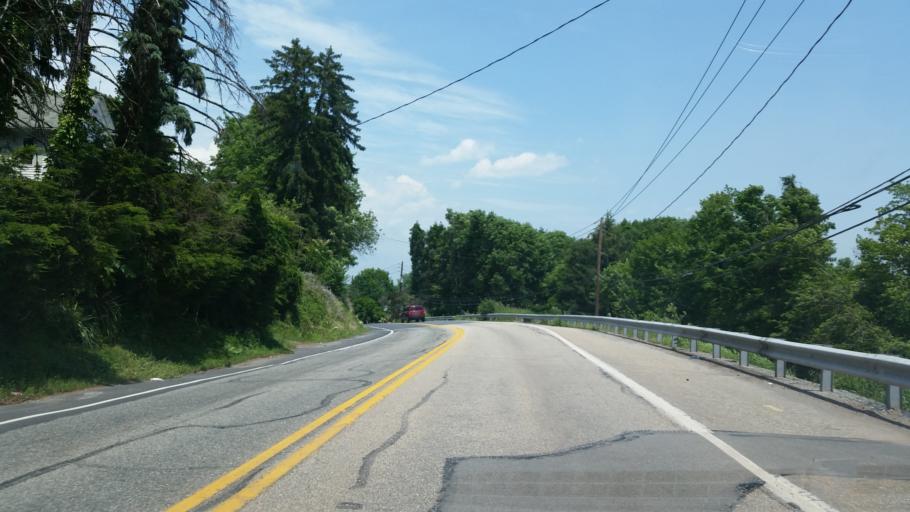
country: US
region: Pennsylvania
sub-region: Cumberland County
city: New Cumberland
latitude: 40.2115
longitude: -76.8676
